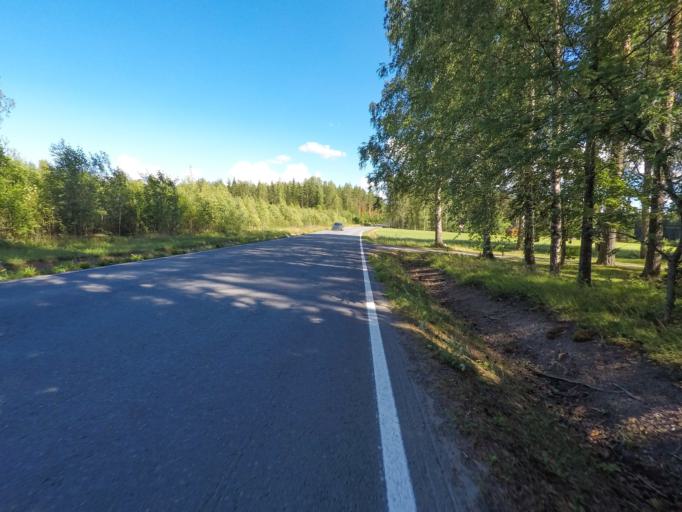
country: FI
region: South Karelia
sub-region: Lappeenranta
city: Taipalsaari
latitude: 61.1791
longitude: 28.0071
